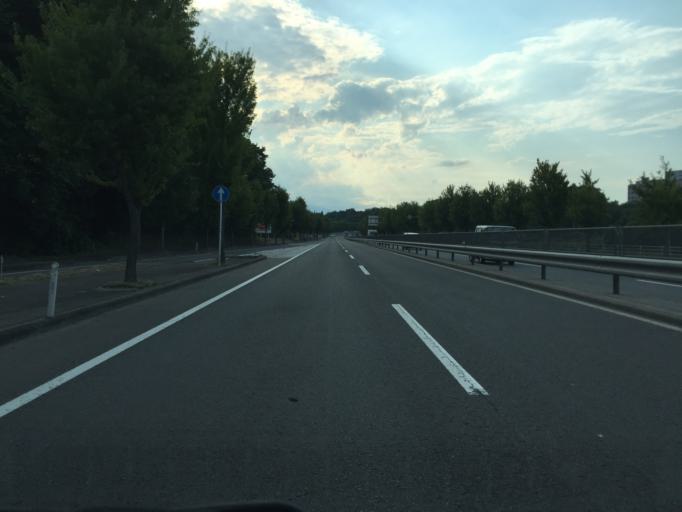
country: JP
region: Fukushima
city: Fukushima-shi
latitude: 37.6847
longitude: 140.4704
